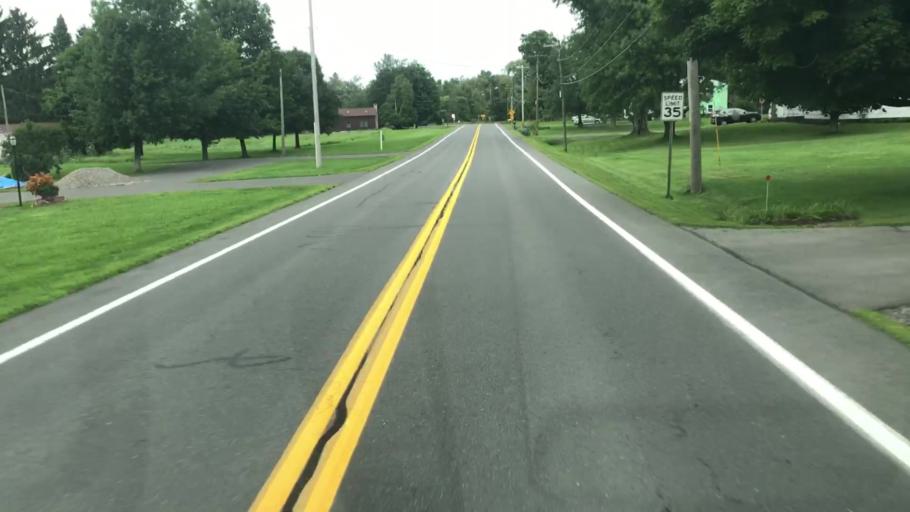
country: US
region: New York
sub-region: Onondaga County
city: Elbridge
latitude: 43.0043
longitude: -76.4575
